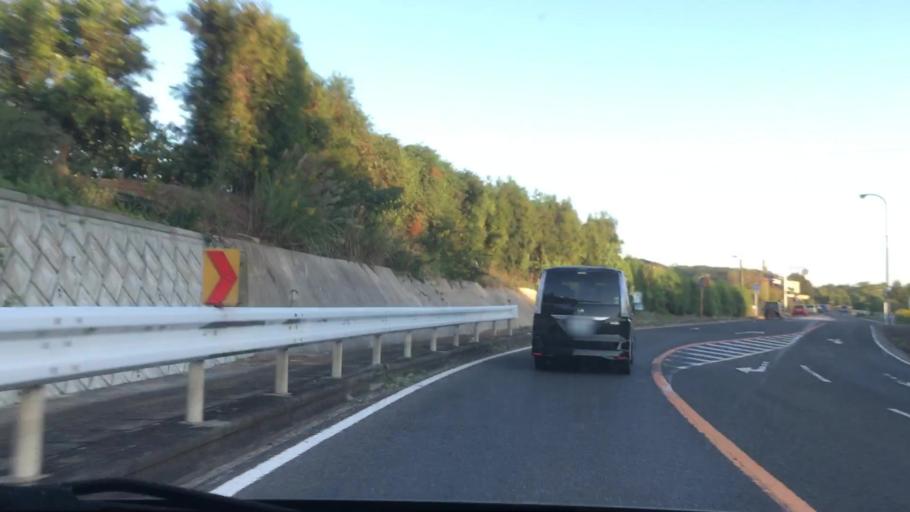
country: JP
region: Nagasaki
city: Sasebo
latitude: 33.0758
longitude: 129.7595
